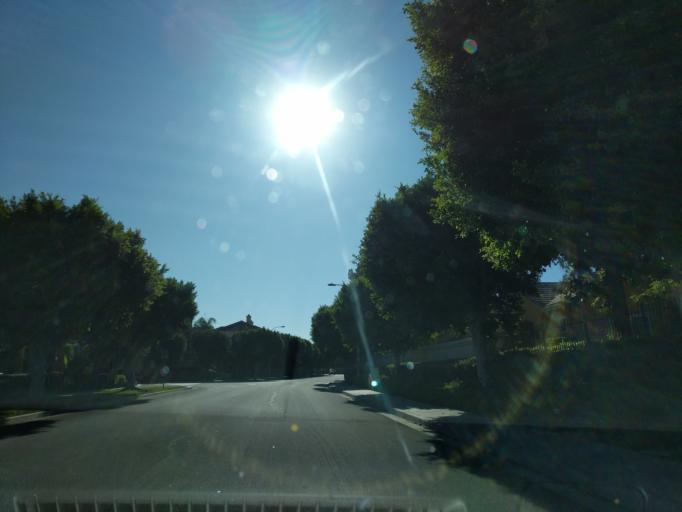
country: US
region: California
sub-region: Orange County
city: Irvine
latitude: 33.6908
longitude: -117.8122
